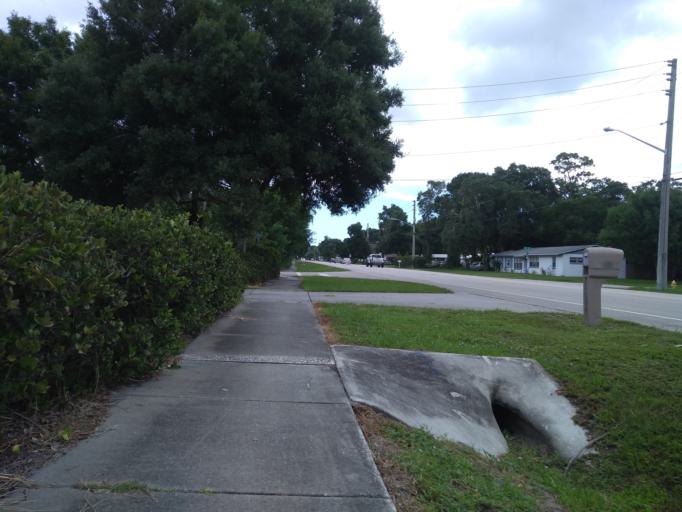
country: US
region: Florida
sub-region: Indian River County
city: Vero Beach
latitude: 27.6342
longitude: -80.4139
